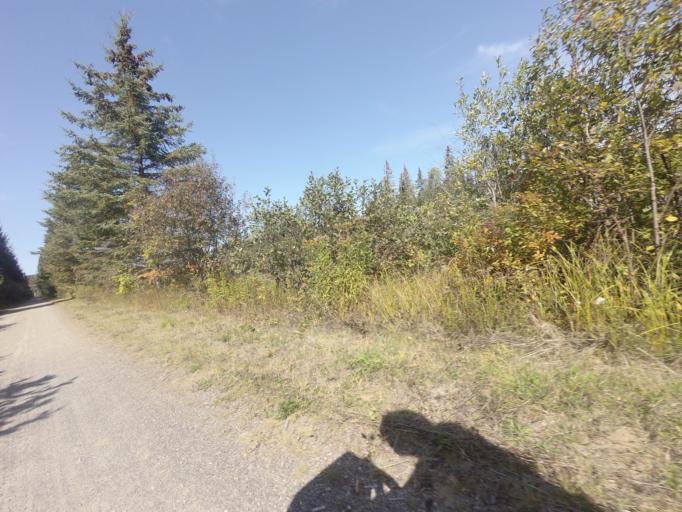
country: CA
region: Quebec
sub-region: Laurentides
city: Sainte-Agathe-des-Monts
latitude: 46.0630
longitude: -74.3038
